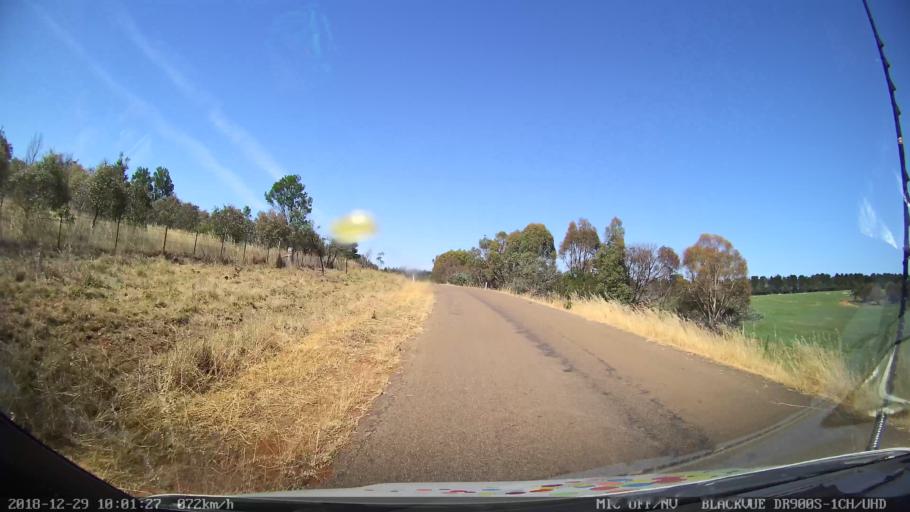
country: AU
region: New South Wales
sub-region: Goulburn Mulwaree
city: Goulburn
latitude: -34.7989
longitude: 149.4760
